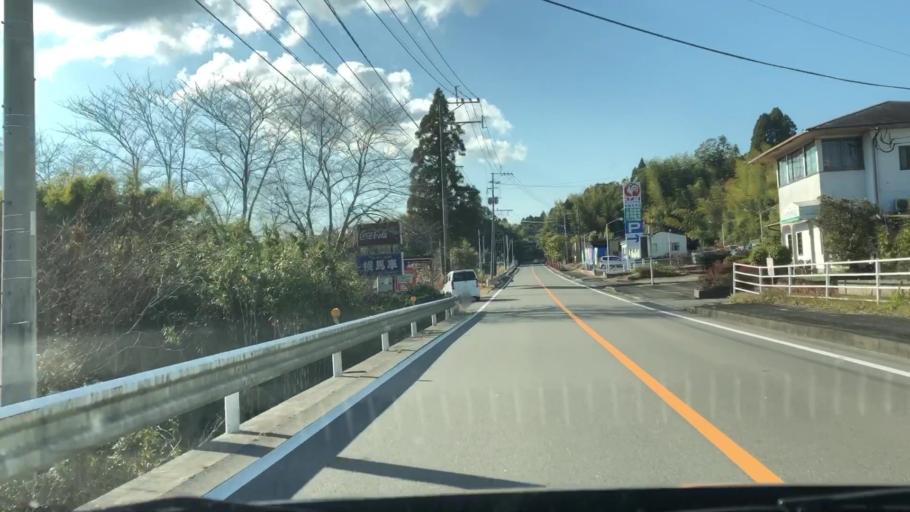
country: JP
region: Kagoshima
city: Satsumasendai
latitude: 31.8585
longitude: 130.3682
